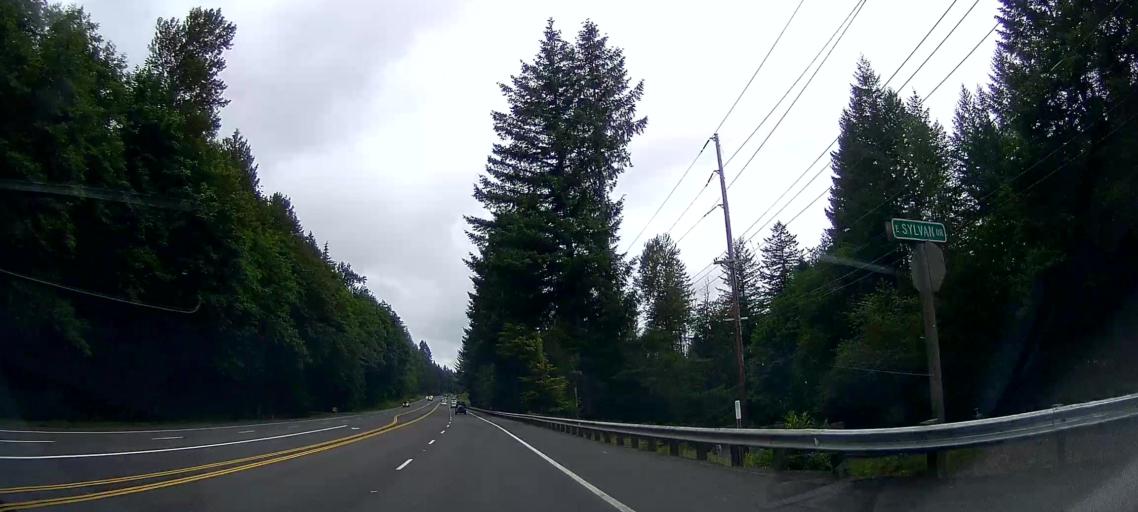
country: US
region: Oregon
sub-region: Clackamas County
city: Mount Hood Village
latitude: 45.3771
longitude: -122.1119
